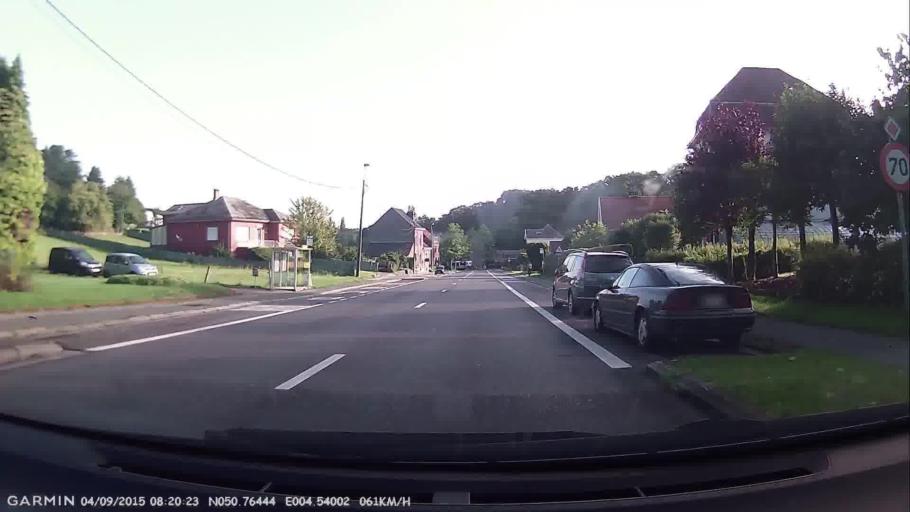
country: BE
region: Flanders
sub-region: Provincie Vlaams-Brabant
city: Overijse
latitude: 50.7646
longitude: 4.5401
